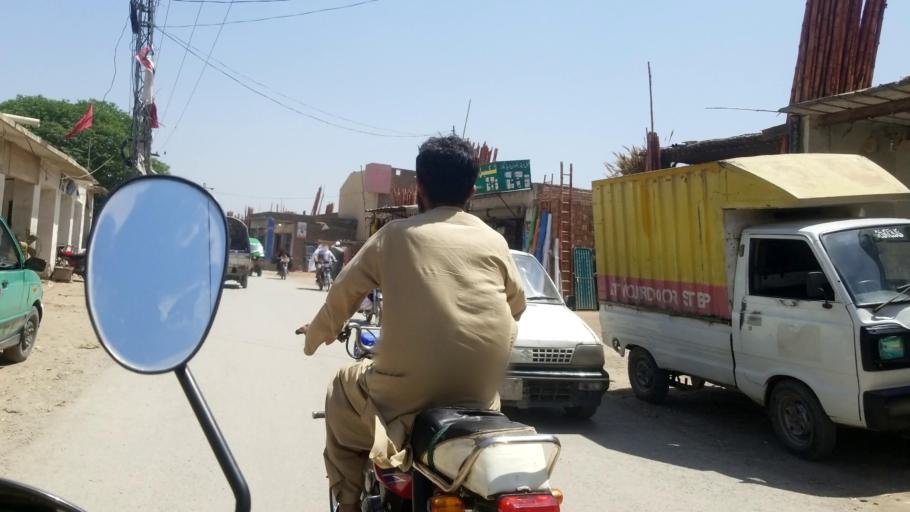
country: PK
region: Khyber Pakhtunkhwa
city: Peshawar
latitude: 34.0301
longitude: 71.4858
